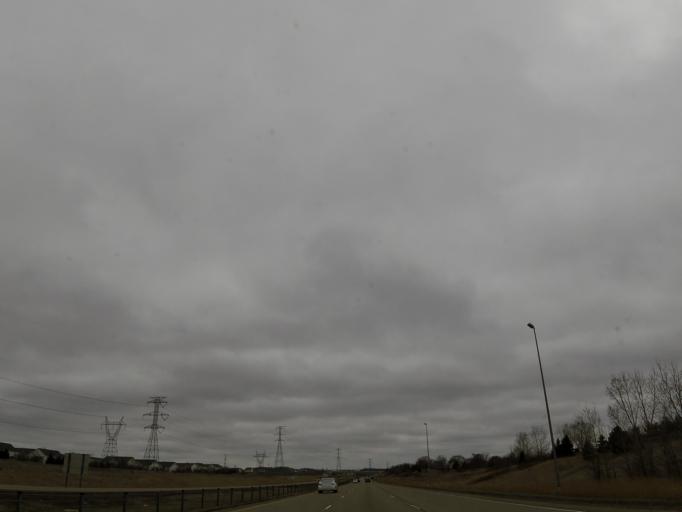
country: US
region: Minnesota
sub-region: Scott County
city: Shakopee
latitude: 44.7775
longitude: -93.5114
